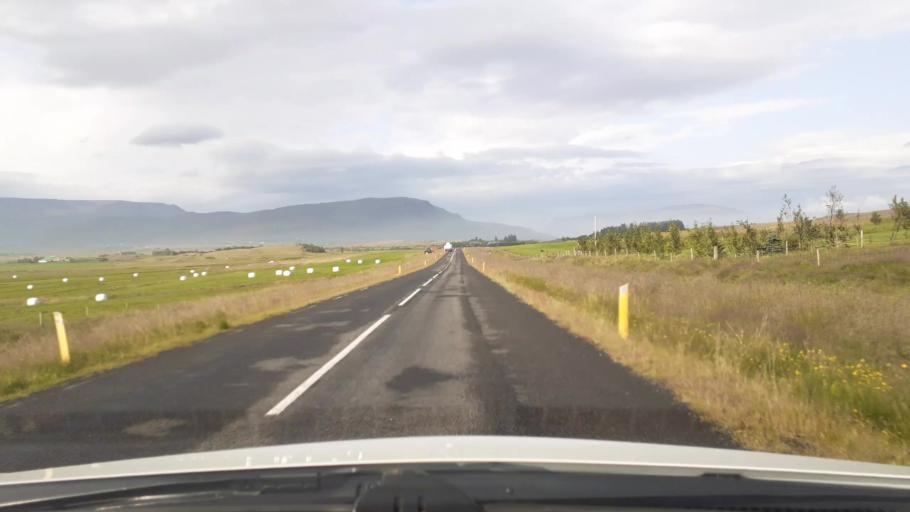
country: IS
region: Capital Region
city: Mosfellsbaer
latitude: 64.3421
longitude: -21.5715
